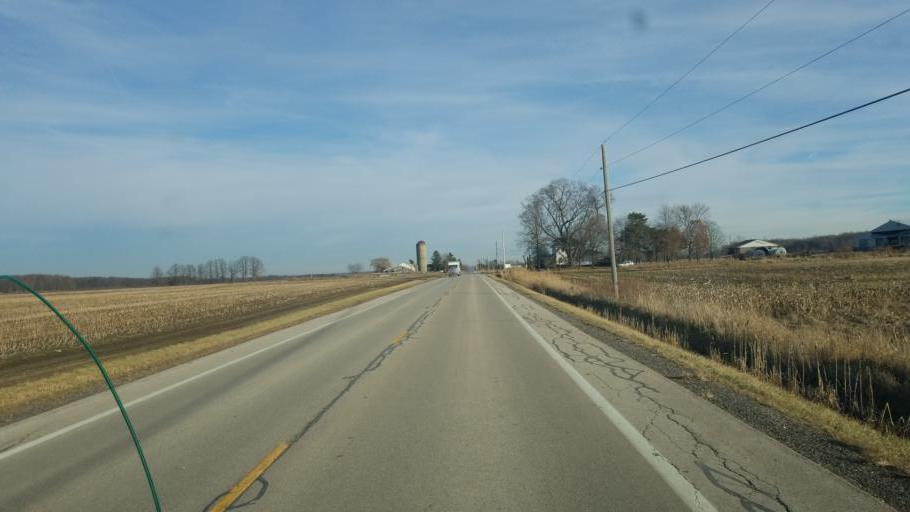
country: US
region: Ohio
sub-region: Ashtabula County
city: Andover
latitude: 41.5355
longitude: -80.6985
